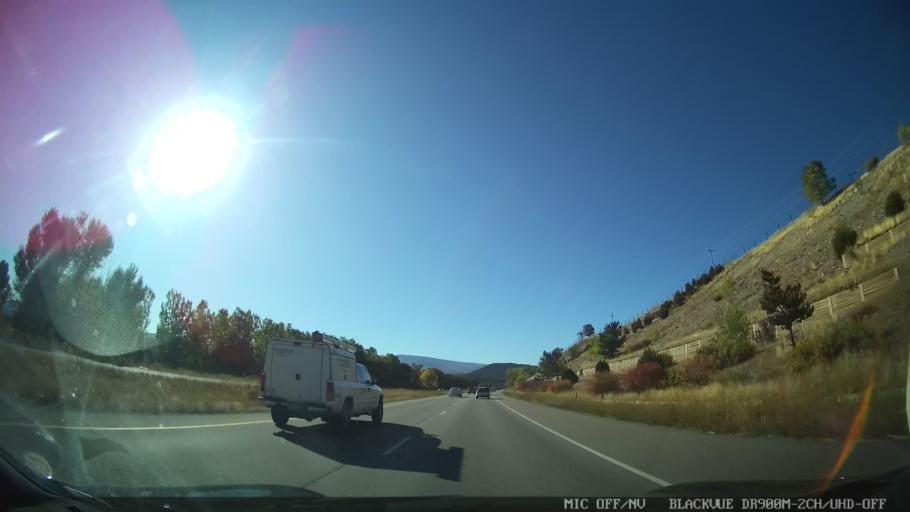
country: US
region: Colorado
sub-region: Garfield County
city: Carbondale
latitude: 39.4120
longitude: -107.1809
